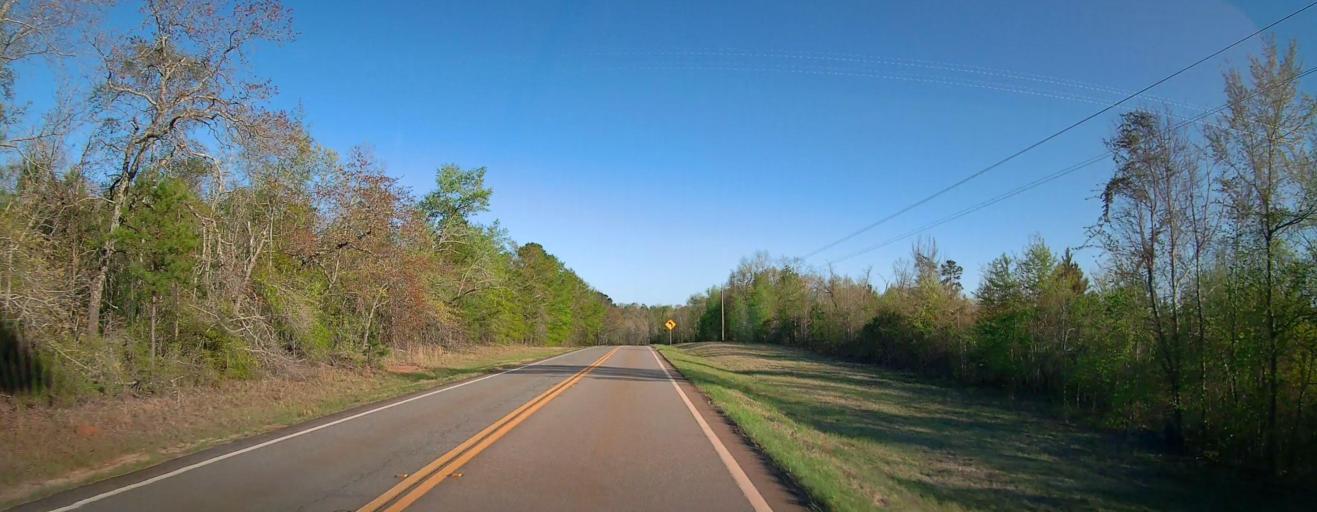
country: US
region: Georgia
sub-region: Wilkinson County
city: Irwinton
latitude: 32.8752
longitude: -83.1230
